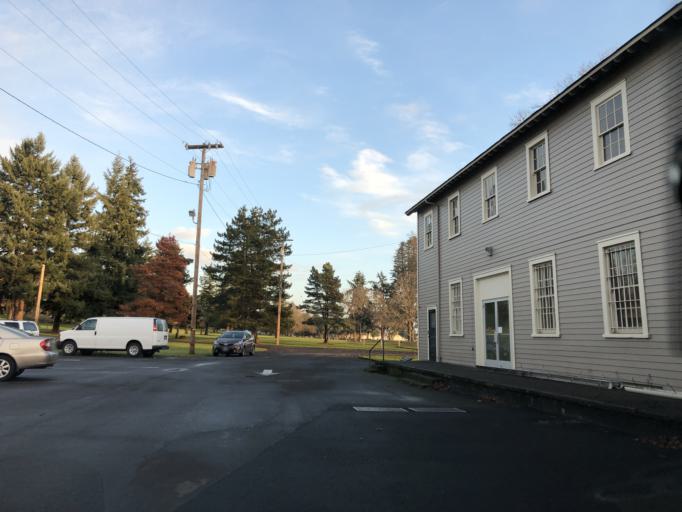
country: US
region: Washington
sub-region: Clark County
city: Vancouver
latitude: 45.6251
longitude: -122.6633
